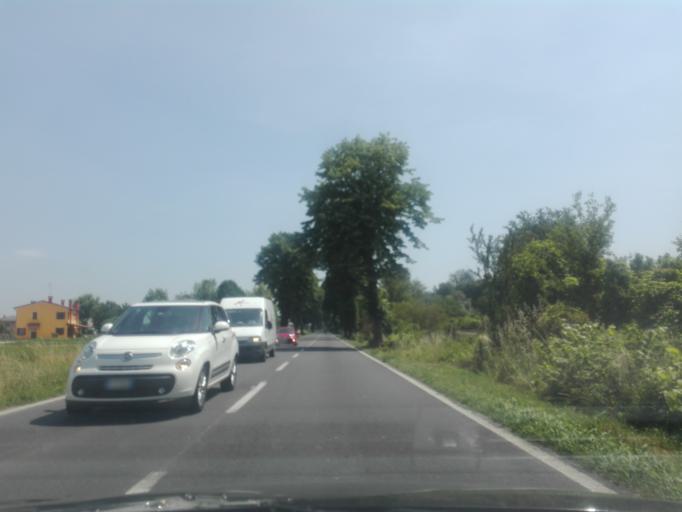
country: IT
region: Veneto
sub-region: Provincia di Rovigo
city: Adria
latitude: 45.0612
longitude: 12.0357
